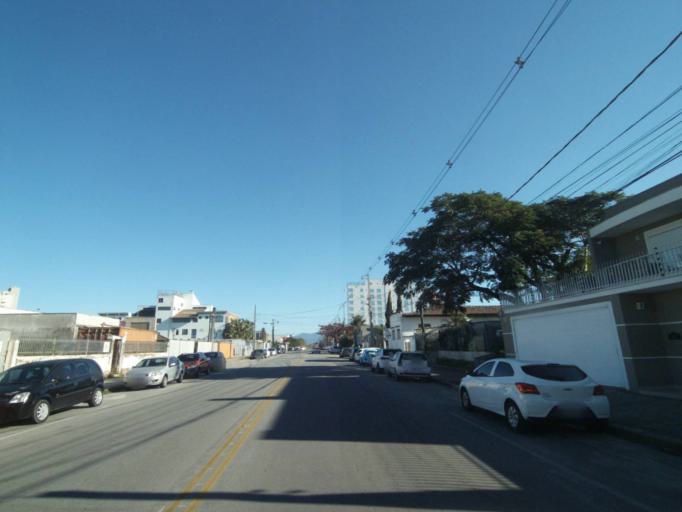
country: BR
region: Parana
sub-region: Paranagua
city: Paranagua
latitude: -25.5164
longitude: -48.5130
